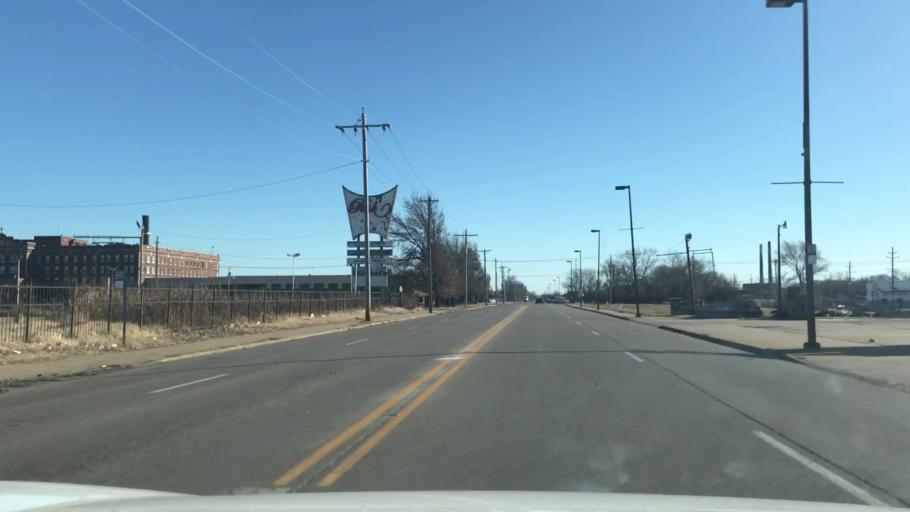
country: US
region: Illinois
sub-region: Saint Clair County
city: East Saint Louis
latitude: 38.6233
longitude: -90.1597
